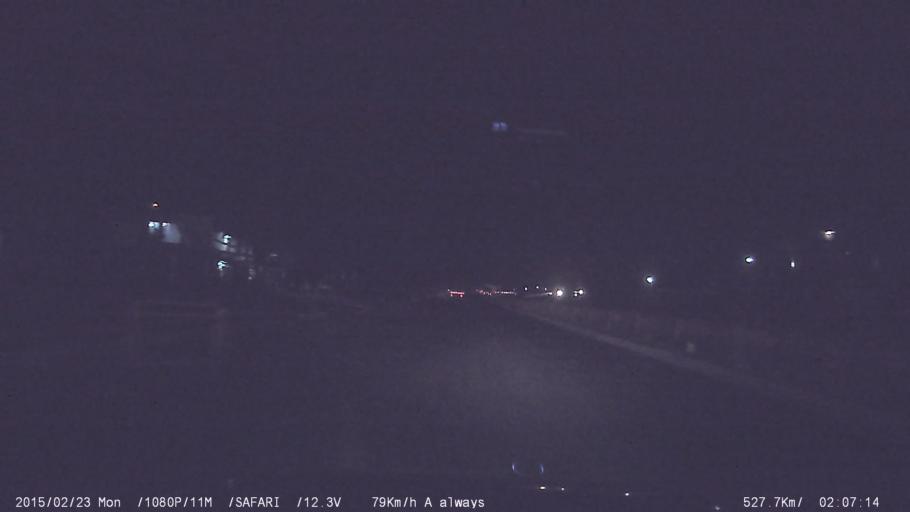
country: IN
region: Tamil Nadu
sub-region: Krishnagiri
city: Kelamangalam
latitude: 12.6617
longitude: 78.0137
